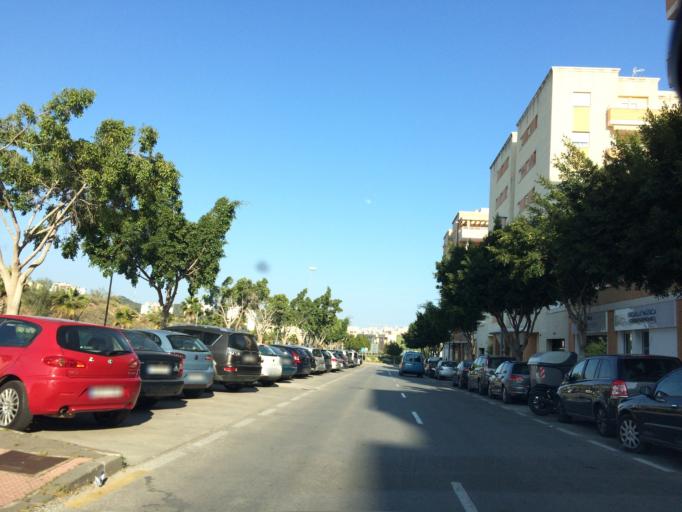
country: ES
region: Andalusia
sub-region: Provincia de Malaga
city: Malaga
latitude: 36.7263
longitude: -4.4744
